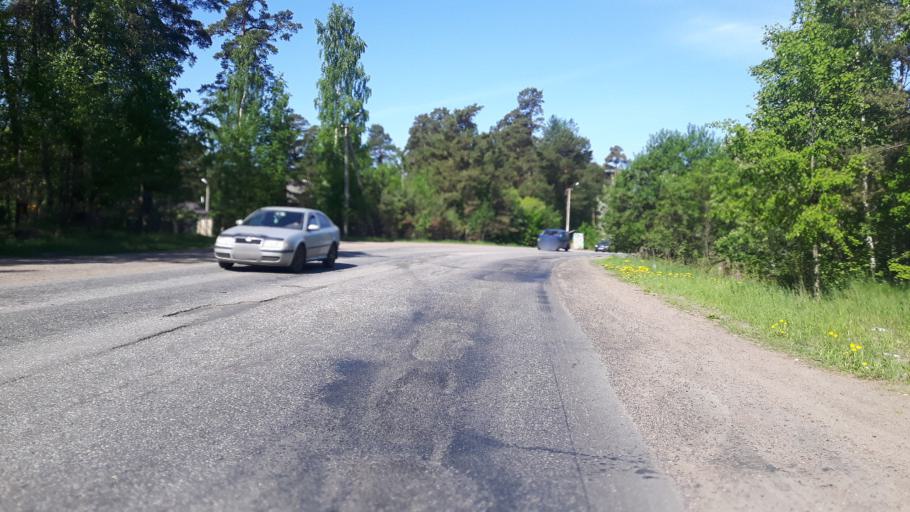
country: RU
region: Leningrad
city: Lebyazh'ye
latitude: 59.9589
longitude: 29.4395
